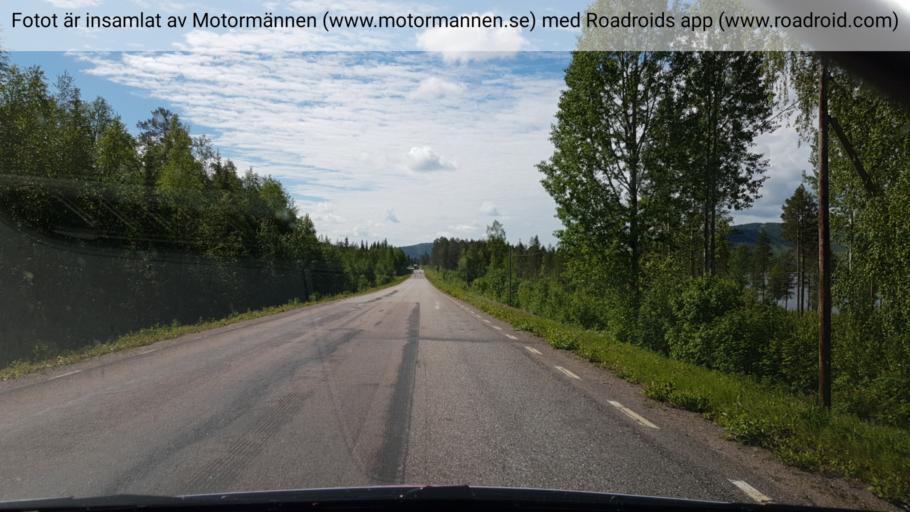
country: FI
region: Lapland
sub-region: Torniolaakso
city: Pello
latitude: 66.6795
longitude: 23.8393
